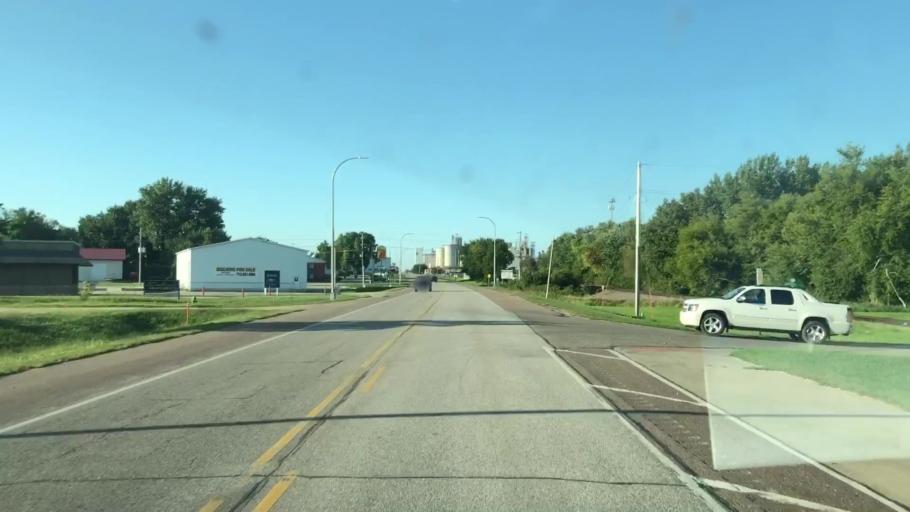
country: US
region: Iowa
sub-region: O'Brien County
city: Sheldon
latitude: 43.1911
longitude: -95.8519
